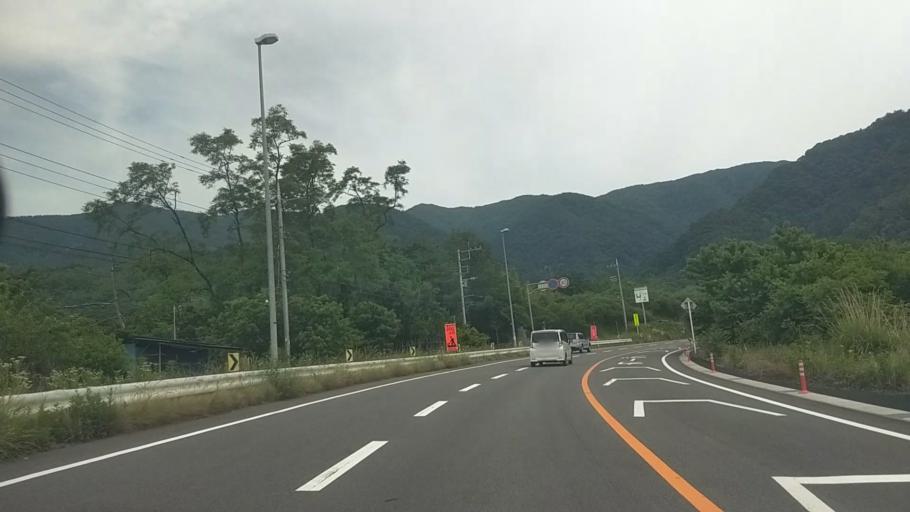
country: JP
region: Yamanashi
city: Isawa
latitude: 35.5702
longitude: 138.5972
